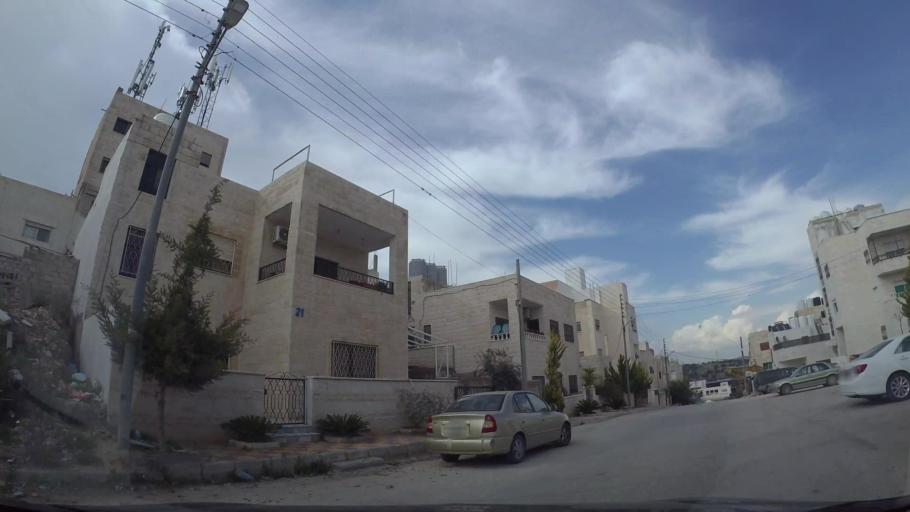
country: JO
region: Amman
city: Amman
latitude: 32.0131
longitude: 35.9444
